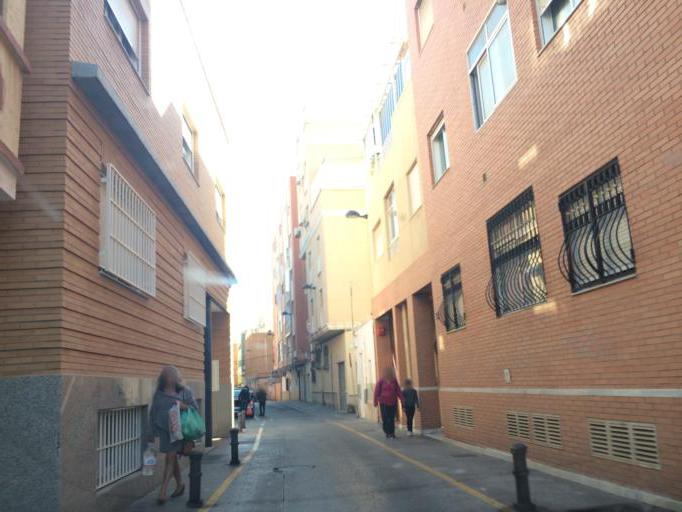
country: ES
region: Andalusia
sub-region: Provincia de Almeria
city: Almeria
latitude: 36.8296
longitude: -2.4534
